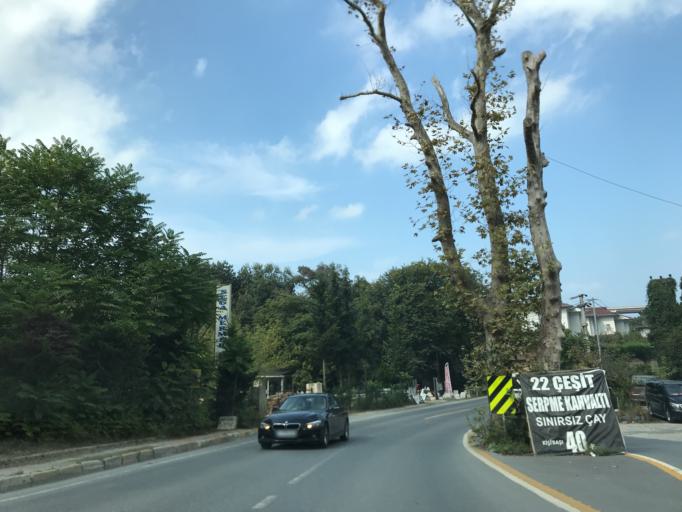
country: TR
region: Istanbul
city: Arikoey
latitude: 41.2208
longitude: 29.0326
